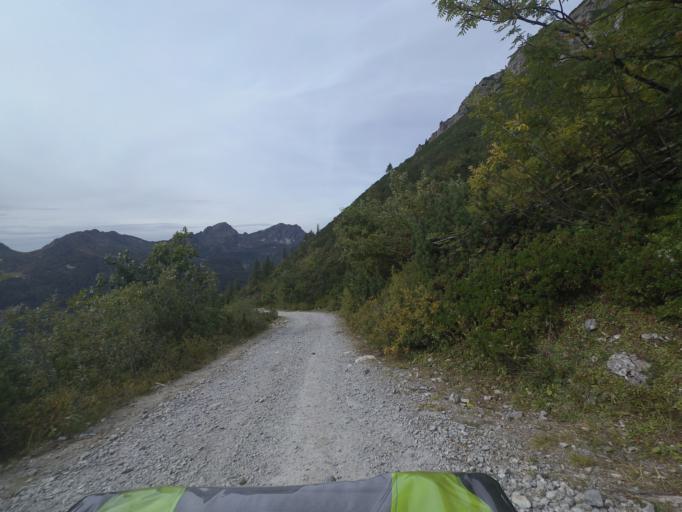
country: AT
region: Salzburg
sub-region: Politischer Bezirk Sankt Johann im Pongau
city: Untertauern
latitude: 47.2903
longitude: 13.5937
